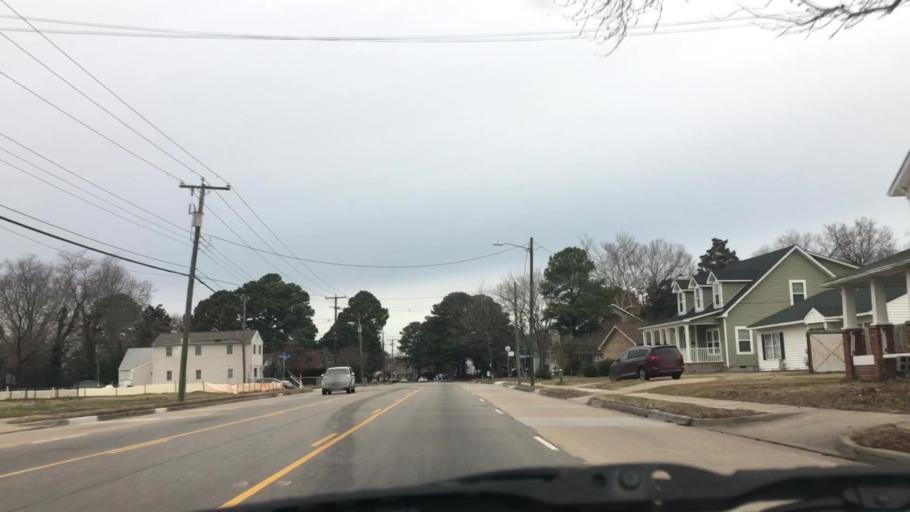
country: US
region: Virginia
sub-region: City of Norfolk
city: Norfolk
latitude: 36.8809
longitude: -76.2337
